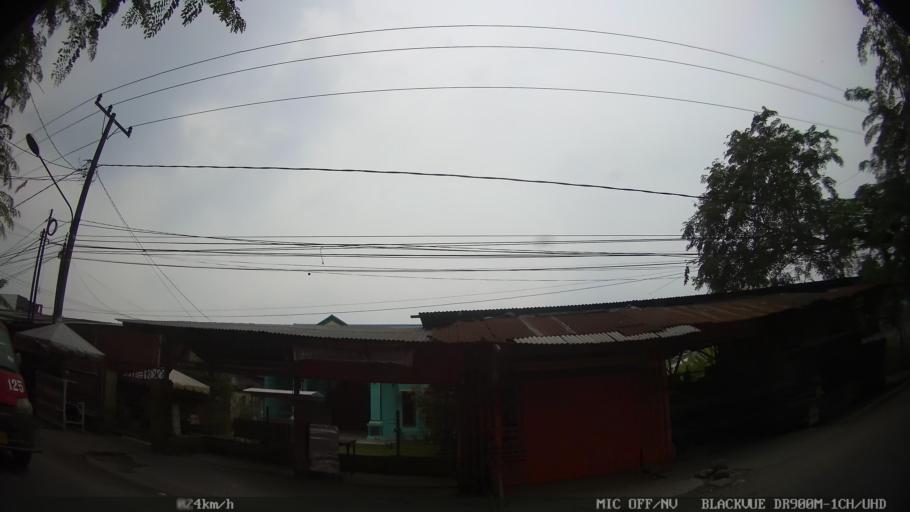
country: ID
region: North Sumatra
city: Deli Tua
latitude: 3.5523
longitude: 98.7121
